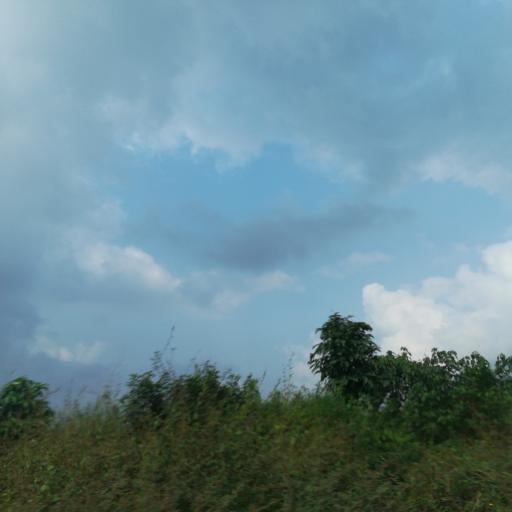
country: NG
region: Rivers
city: Okrika
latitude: 4.8209
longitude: 7.1252
